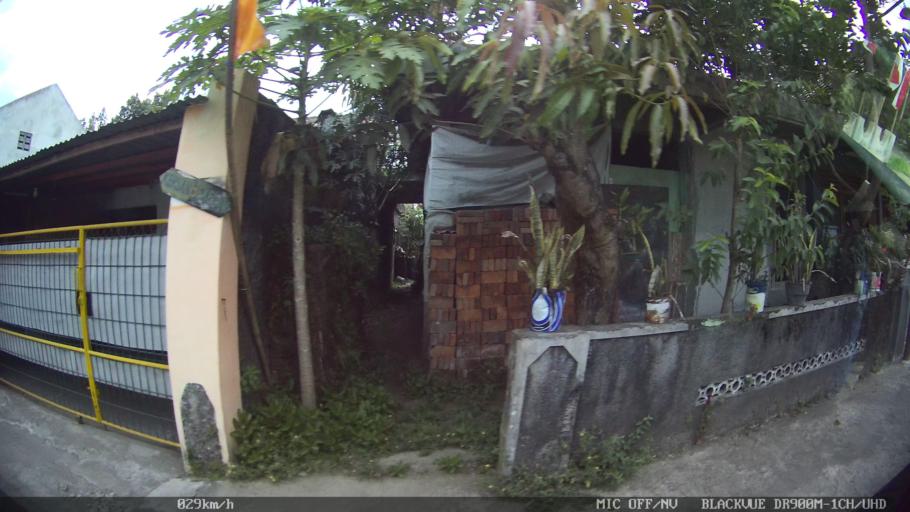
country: ID
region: Daerah Istimewa Yogyakarta
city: Kasihan
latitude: -7.8179
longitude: 110.3401
